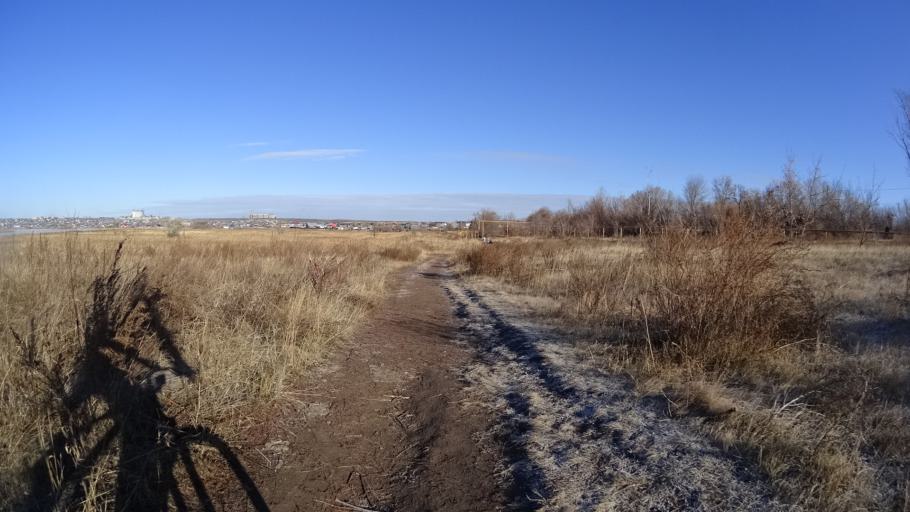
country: RU
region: Chelyabinsk
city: Troitsk
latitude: 54.0809
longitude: 61.5903
